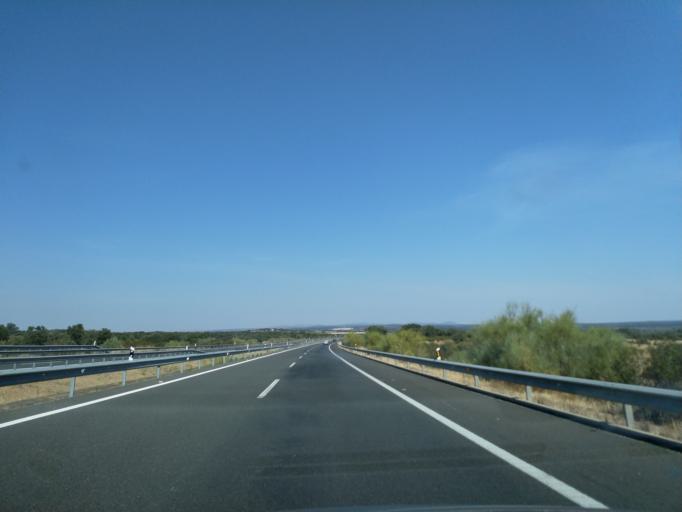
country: ES
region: Extremadura
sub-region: Provincia de Caceres
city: Alcuescar
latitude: 39.1828
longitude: -6.2750
